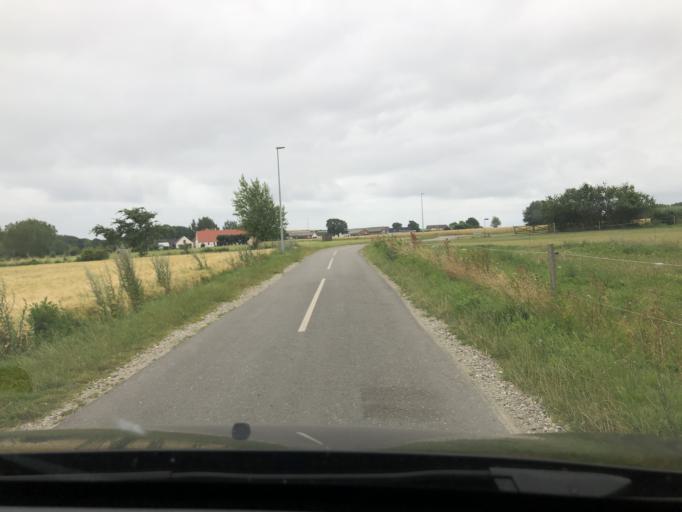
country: DK
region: South Denmark
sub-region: AEro Kommune
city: Marstal
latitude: 54.8513
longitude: 10.4758
